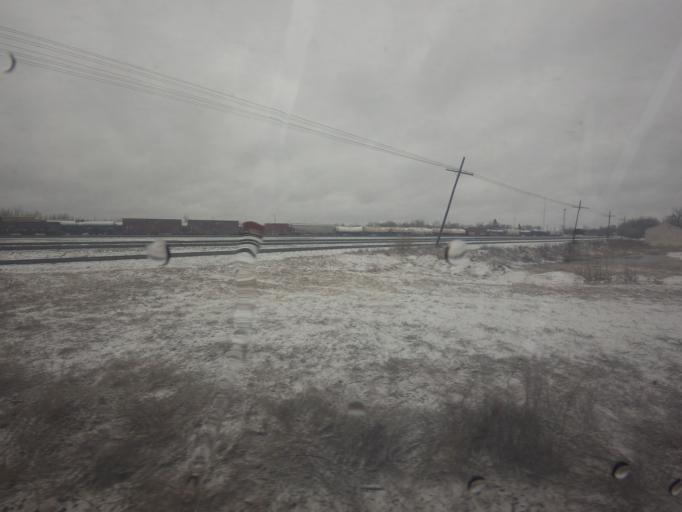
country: CA
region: Ontario
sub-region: Lanark County
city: Smiths Falls
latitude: 44.9045
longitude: -76.0149
